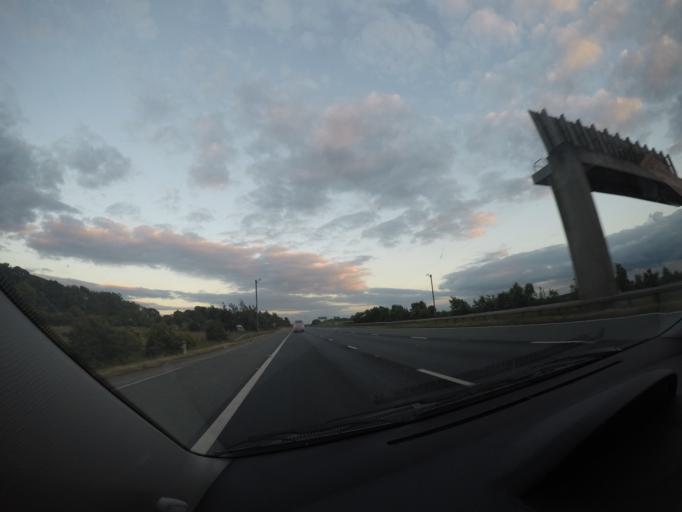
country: GB
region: England
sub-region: North Yorkshire
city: Boroughbridge
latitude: 54.0701
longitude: -1.3922
